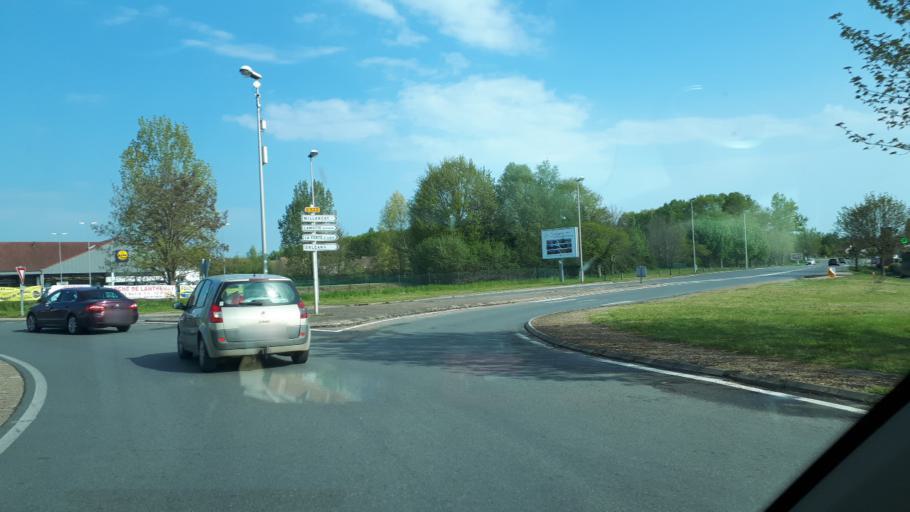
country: FR
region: Centre
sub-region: Departement du Loir-et-Cher
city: Romorantin-Lanthenay
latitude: 47.3772
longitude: 1.7362
